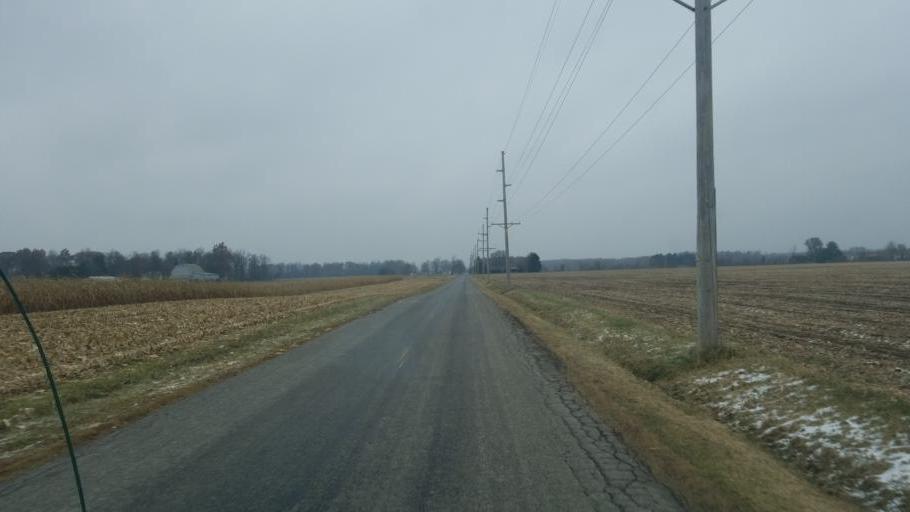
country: US
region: Ohio
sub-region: Richland County
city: Shelby
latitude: 40.9257
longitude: -82.6860
